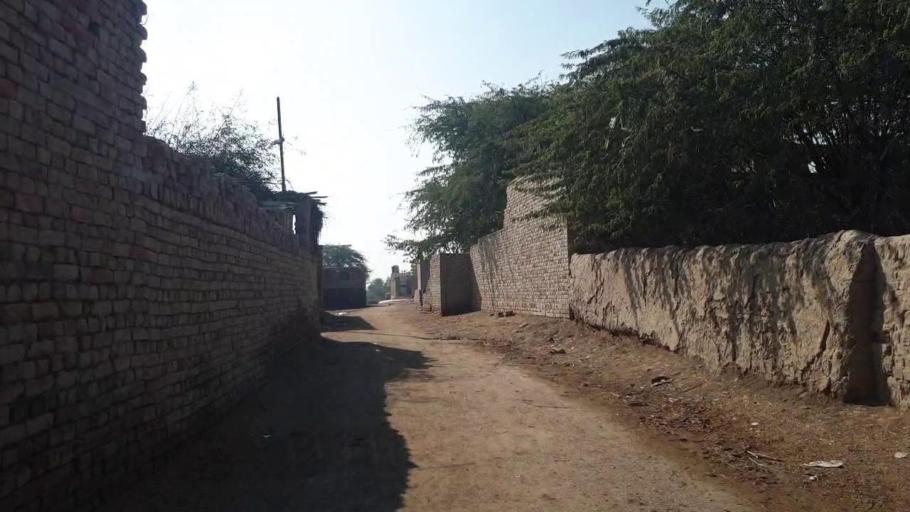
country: PK
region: Sindh
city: Shahdadpur
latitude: 25.9631
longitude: 68.5791
